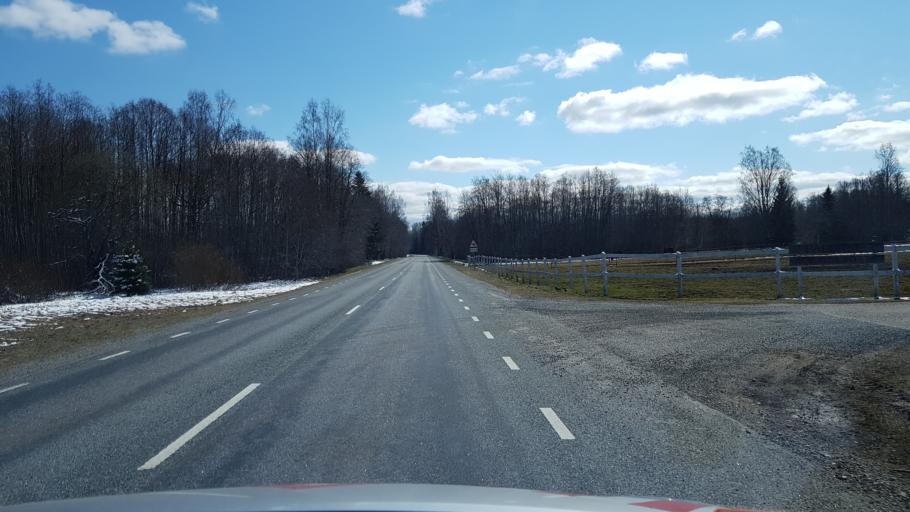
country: EE
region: Laeaene-Virumaa
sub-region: Tapa vald
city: Tapa
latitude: 59.4414
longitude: 25.9556
